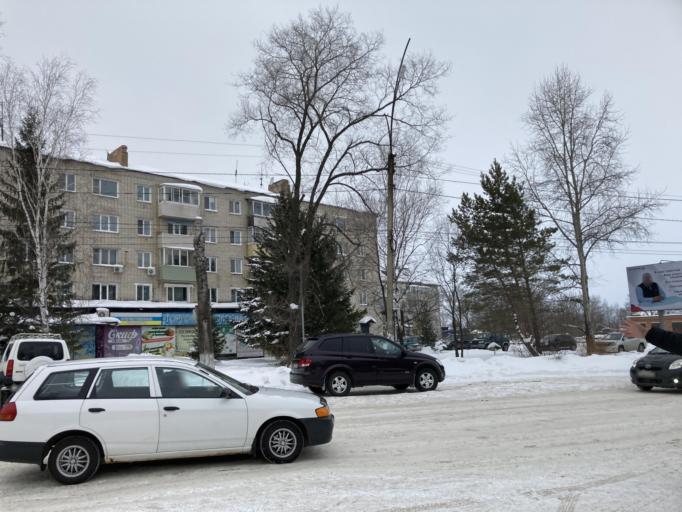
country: RU
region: Khabarovsk Krai
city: Khor
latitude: 47.9700
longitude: 135.0521
